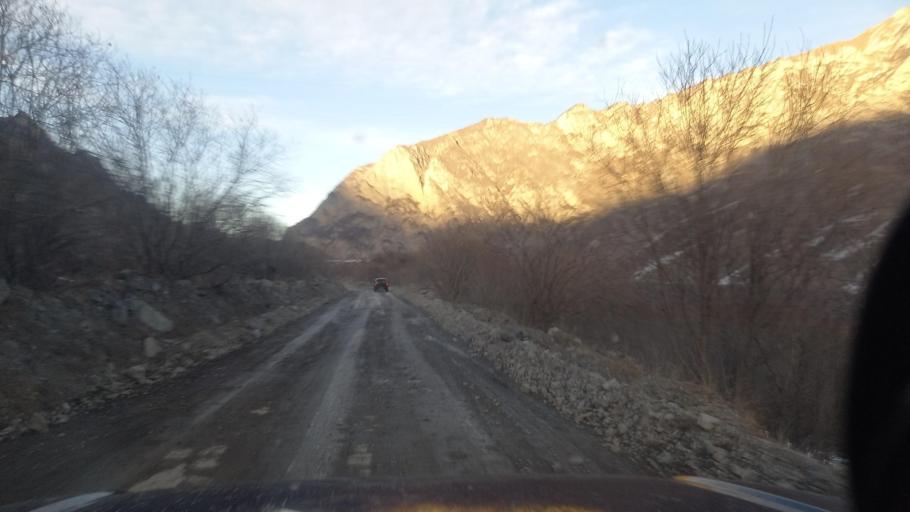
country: RU
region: Ingushetiya
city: Dzhayrakh
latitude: 42.8429
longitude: 44.5149
